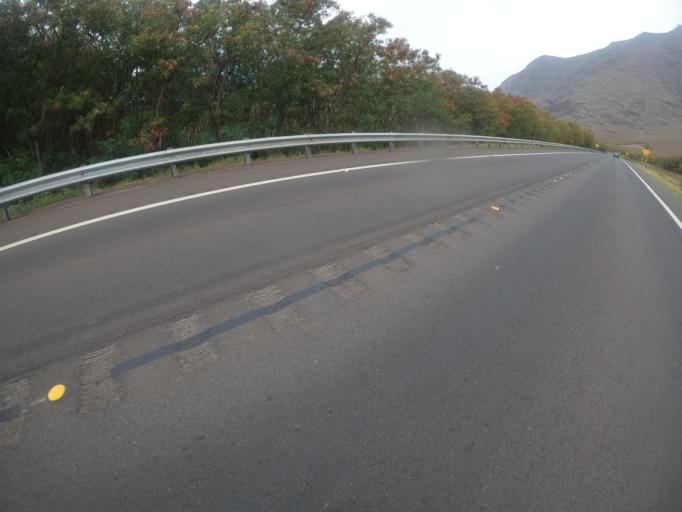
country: US
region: Hawaii
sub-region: Honolulu County
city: Makaha Valley
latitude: 21.5317
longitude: -158.2282
